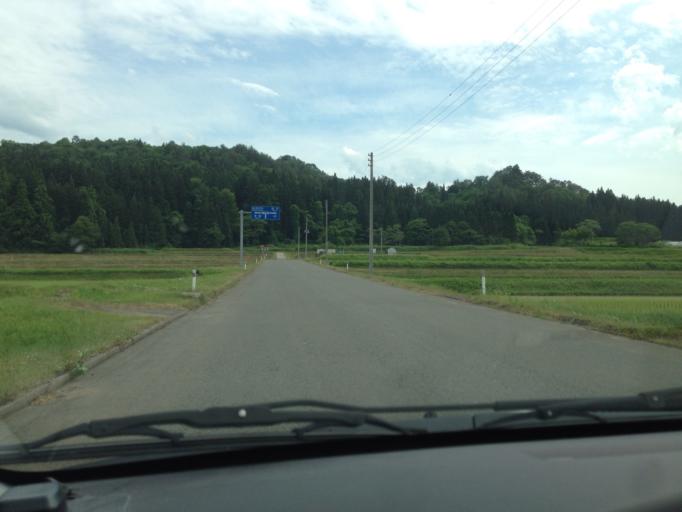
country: JP
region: Fukushima
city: Kitakata
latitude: 37.5032
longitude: 139.7179
